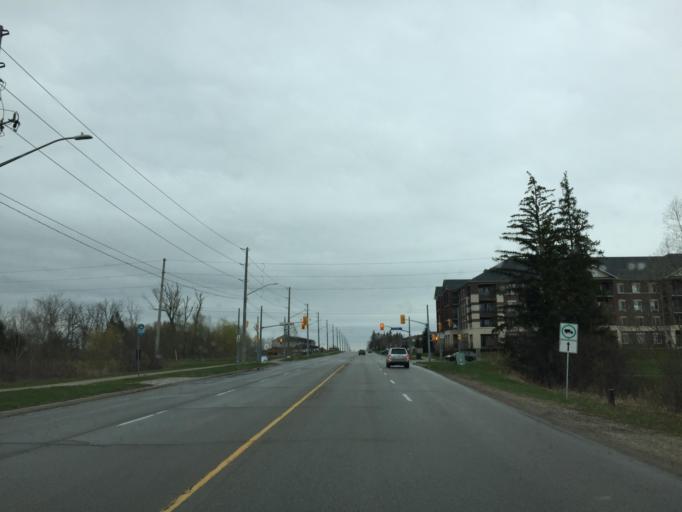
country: CA
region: Ontario
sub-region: Wellington County
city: Guelph
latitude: 43.5742
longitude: -80.2189
